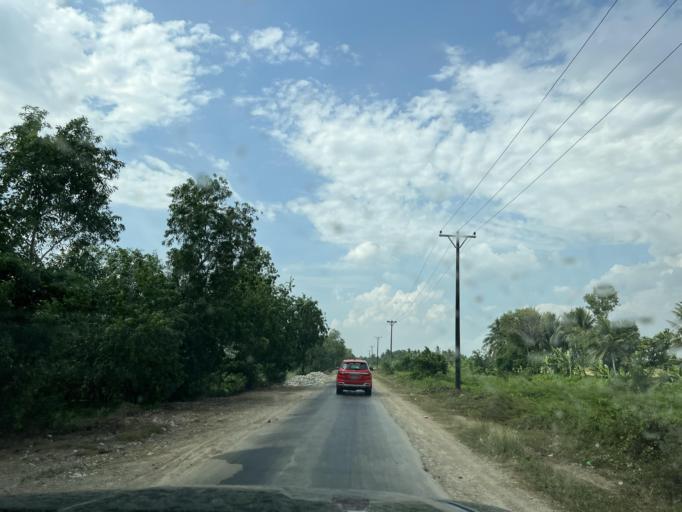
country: MM
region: Ayeyarwady
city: Pyapon
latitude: 16.2469
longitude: 95.7003
